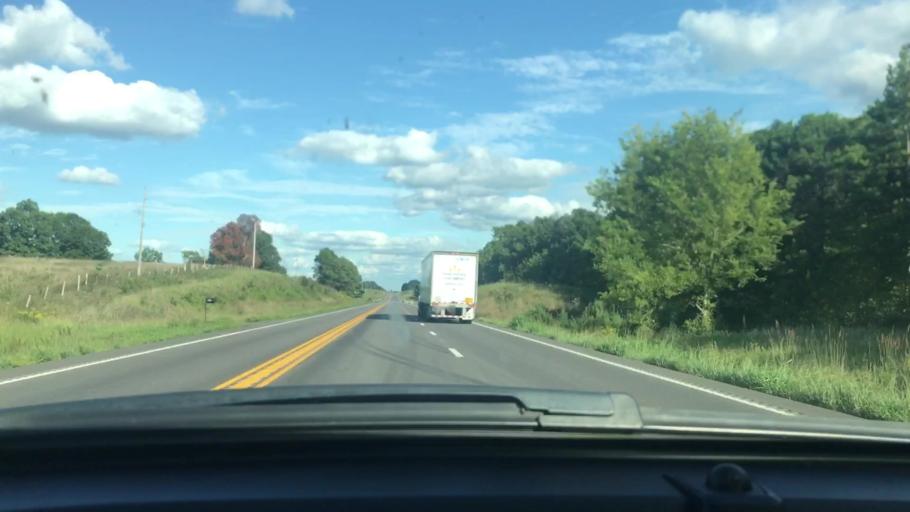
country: US
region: Missouri
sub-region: Oregon County
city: Thayer
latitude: 36.5872
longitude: -91.6307
